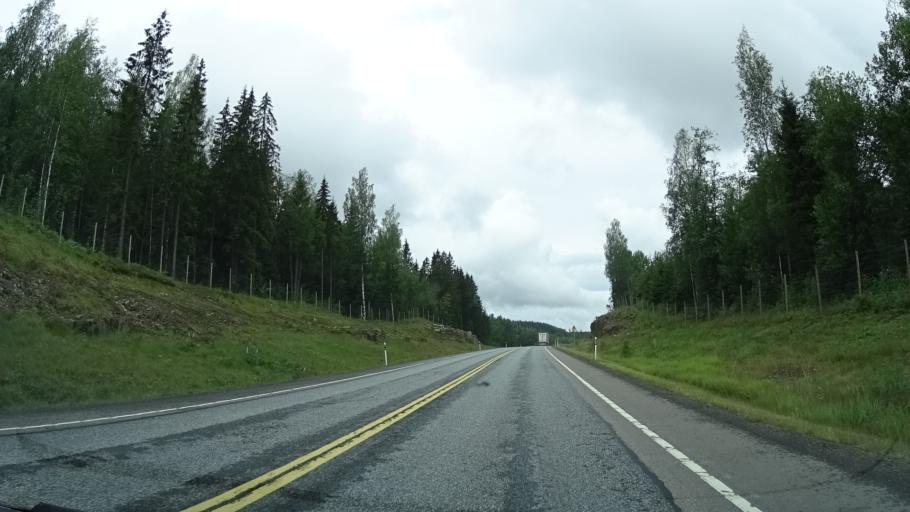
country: FI
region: Uusimaa
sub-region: Helsinki
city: Karkkila
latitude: 60.5758
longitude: 24.1431
